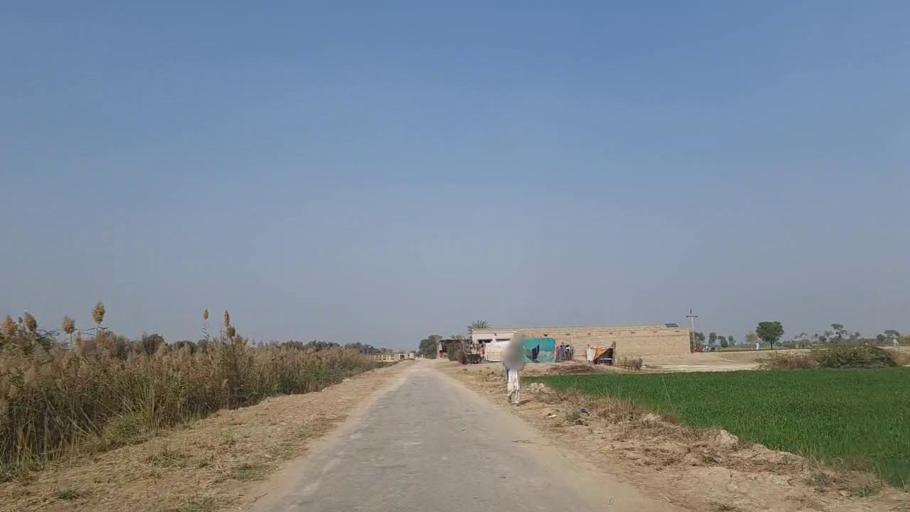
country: PK
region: Sindh
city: Daur
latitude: 26.4746
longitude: 68.4659
